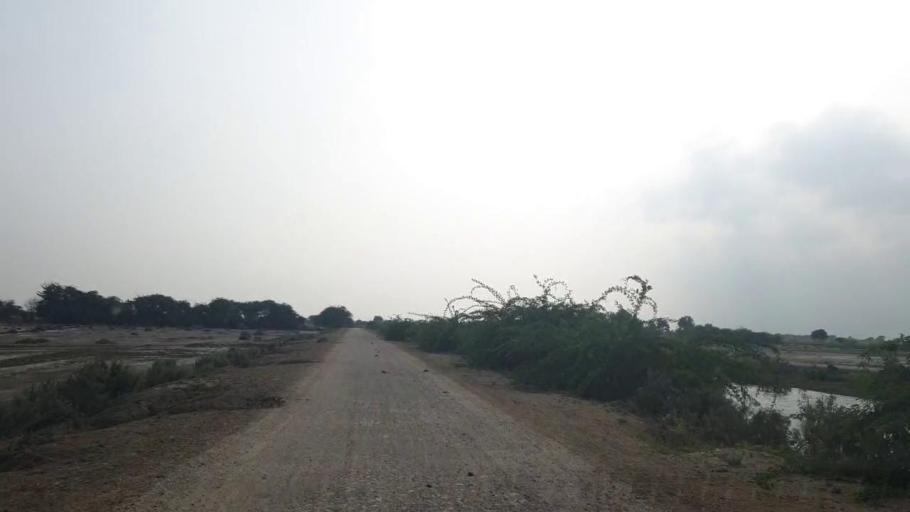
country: PK
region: Sindh
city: Badin
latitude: 24.6281
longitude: 68.6918
